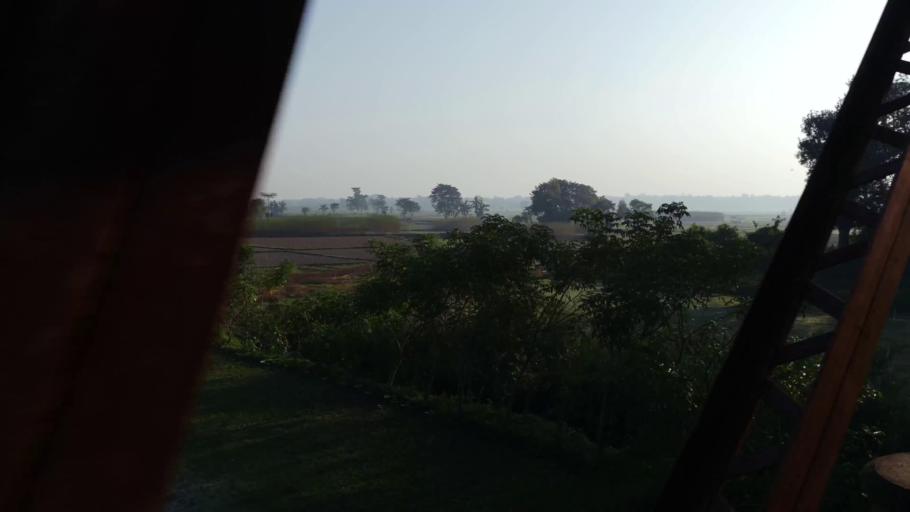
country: BD
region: Dhaka
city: Jamalpur
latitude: 24.9216
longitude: 89.9408
